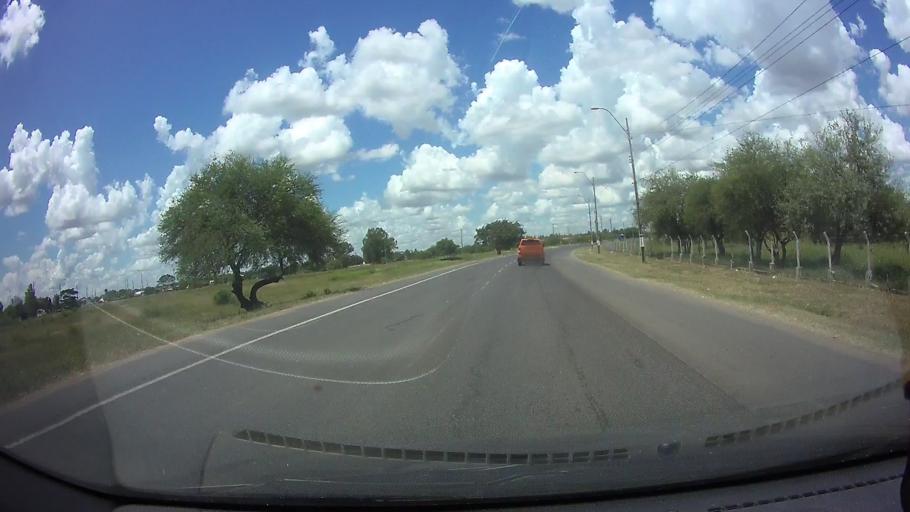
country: PY
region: Central
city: Colonia Mariano Roque Alonso
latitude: -25.1717
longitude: -57.5660
